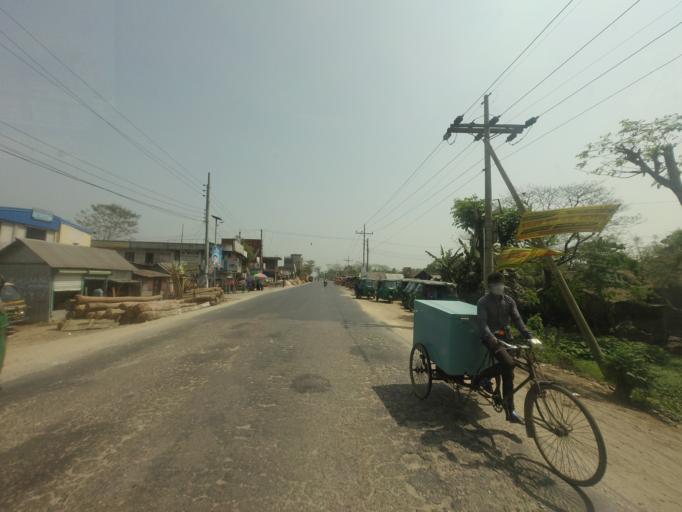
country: BD
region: Dhaka
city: Bhairab Bazar
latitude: 24.0544
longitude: 91.1473
